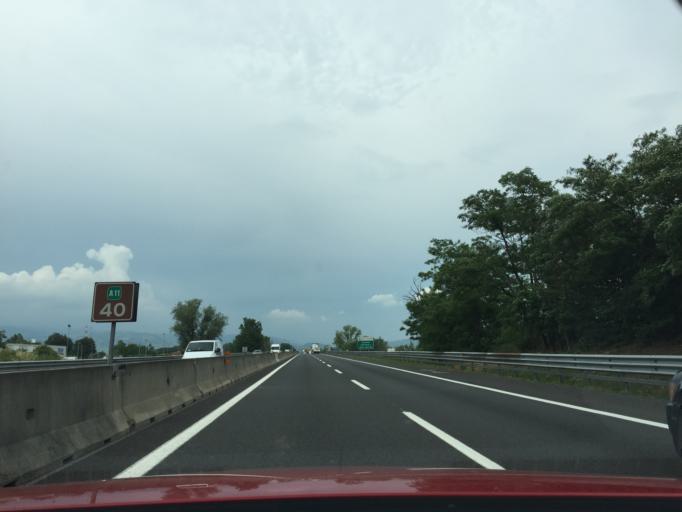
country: IT
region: Tuscany
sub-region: Provincia di Pistoia
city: Chiesina Uzzanese
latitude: 43.8318
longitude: 10.7023
